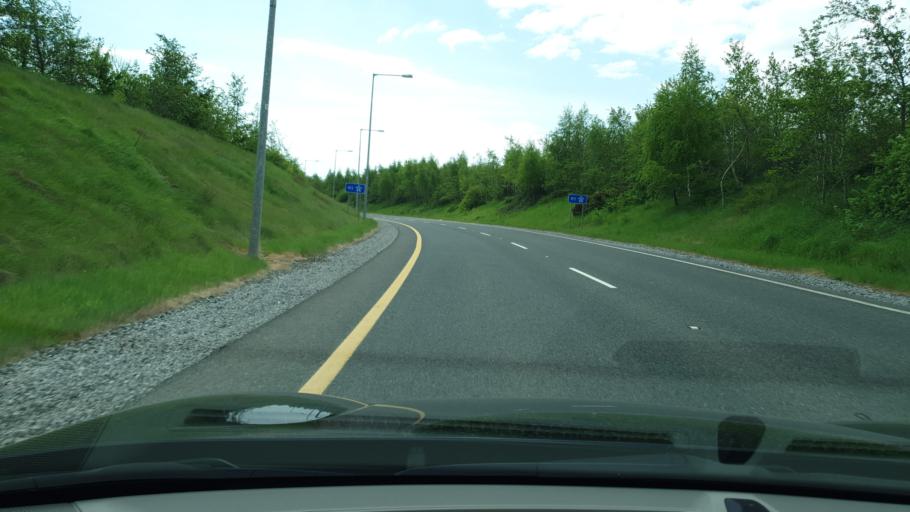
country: IE
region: Leinster
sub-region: An Mhi
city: Navan
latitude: 53.6199
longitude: -6.6765
